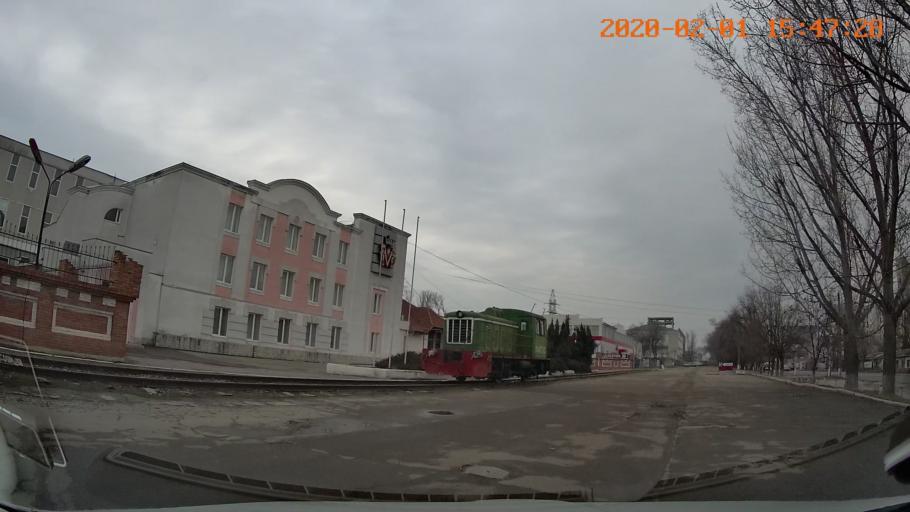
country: MD
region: Chisinau
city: Chisinau
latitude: 47.0214
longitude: 28.8684
